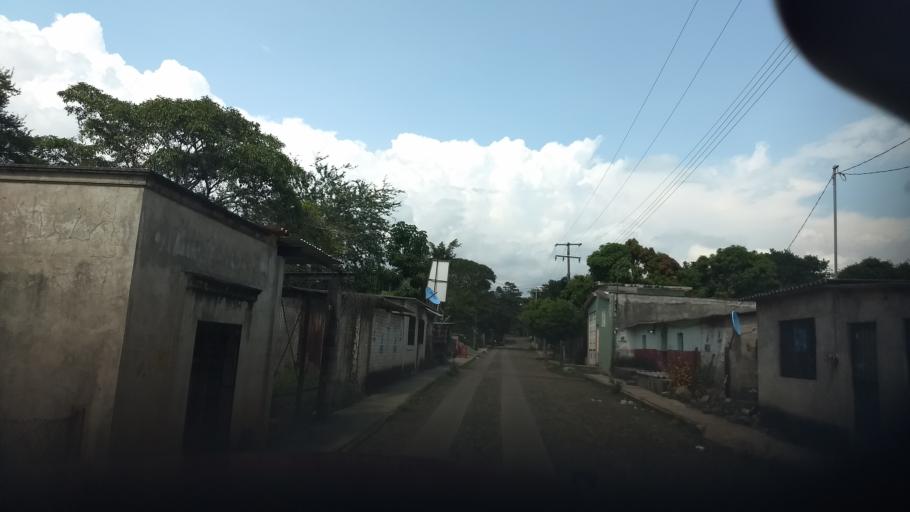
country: MX
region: Jalisco
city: Tonila
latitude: 19.4074
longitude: -103.4851
